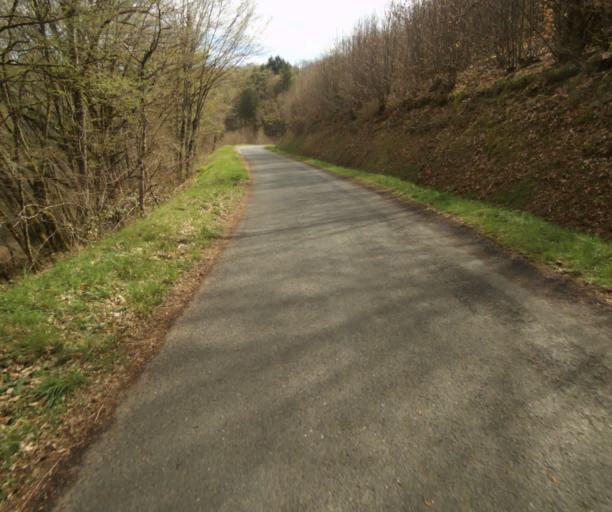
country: FR
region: Limousin
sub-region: Departement de la Correze
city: Laguenne
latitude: 45.2515
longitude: 1.8306
